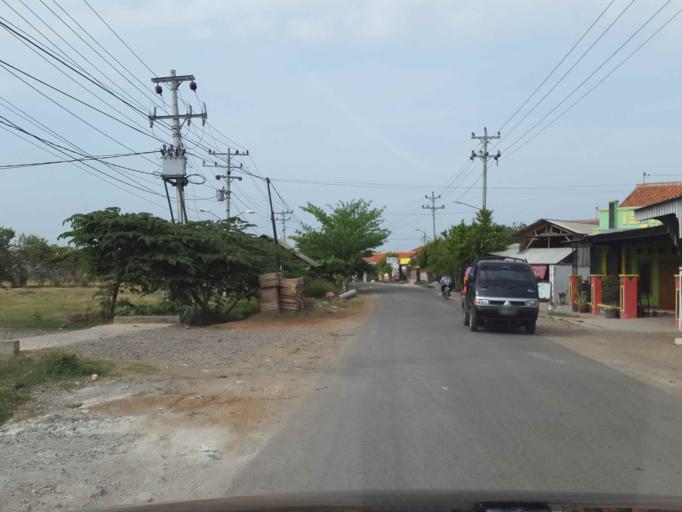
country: ID
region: Central Java
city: Bulakamba
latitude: -6.8655
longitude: 109.0103
